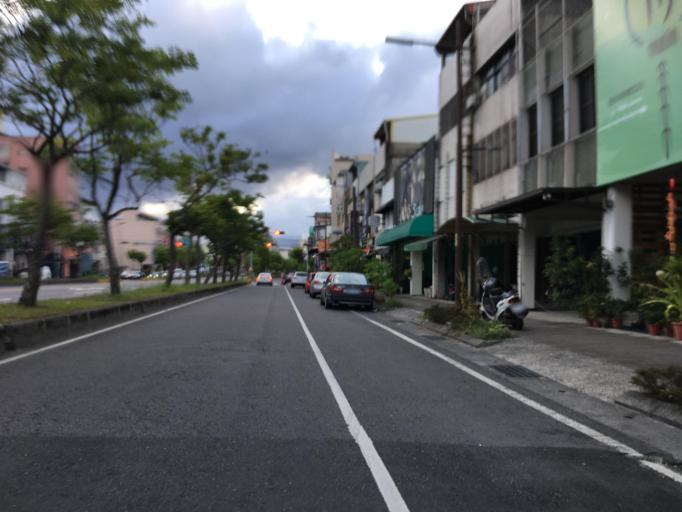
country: TW
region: Taiwan
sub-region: Yilan
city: Yilan
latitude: 24.6685
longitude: 121.7675
